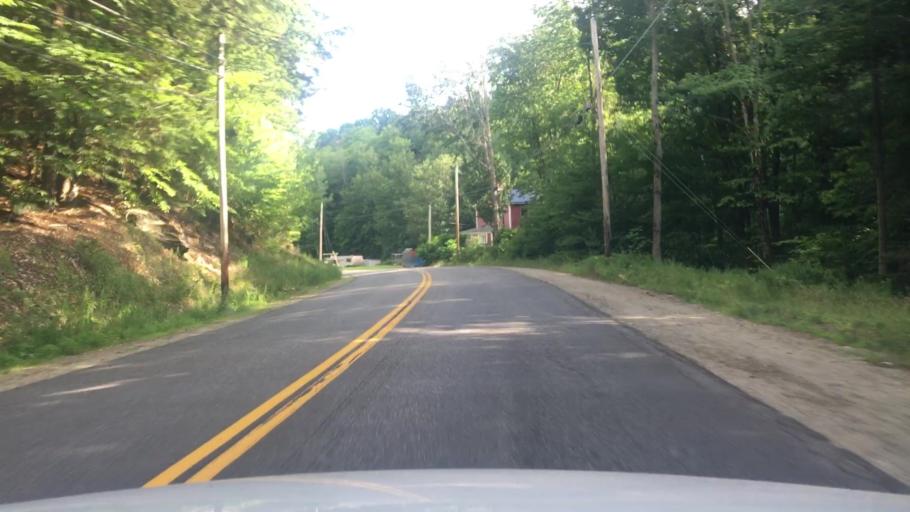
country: US
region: Maine
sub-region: Franklin County
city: Wilton
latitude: 44.5760
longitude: -70.2322
